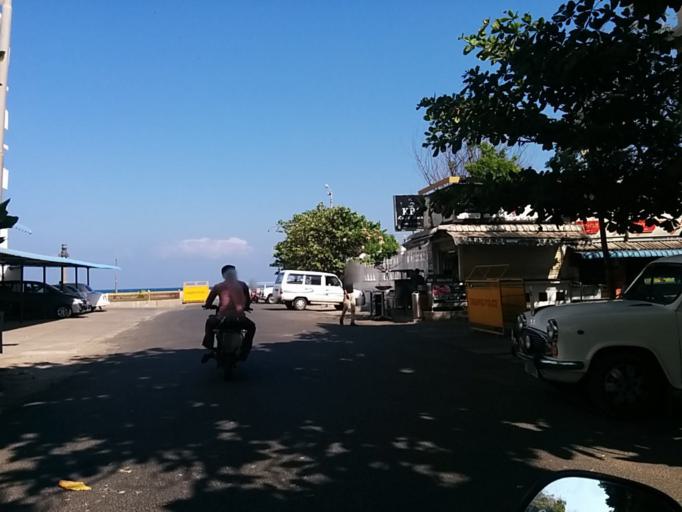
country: IN
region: Pondicherry
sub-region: Puducherry
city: Puducherry
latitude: 11.9357
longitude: 79.8358
